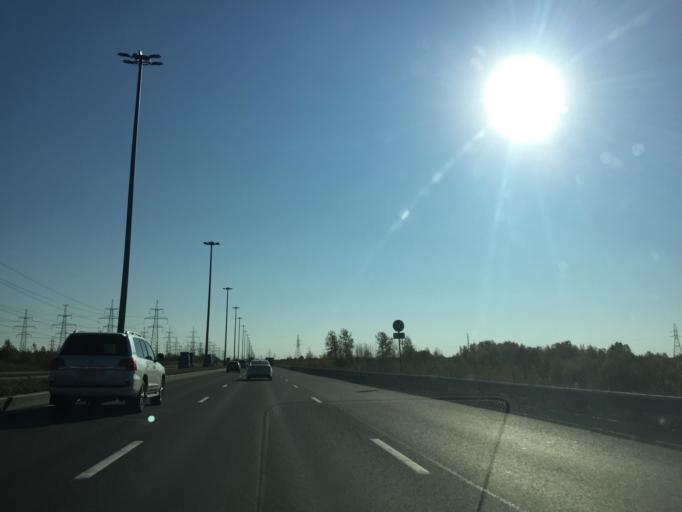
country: RU
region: St.-Petersburg
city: Petro-Slavyanka
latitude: 59.7628
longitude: 30.5077
